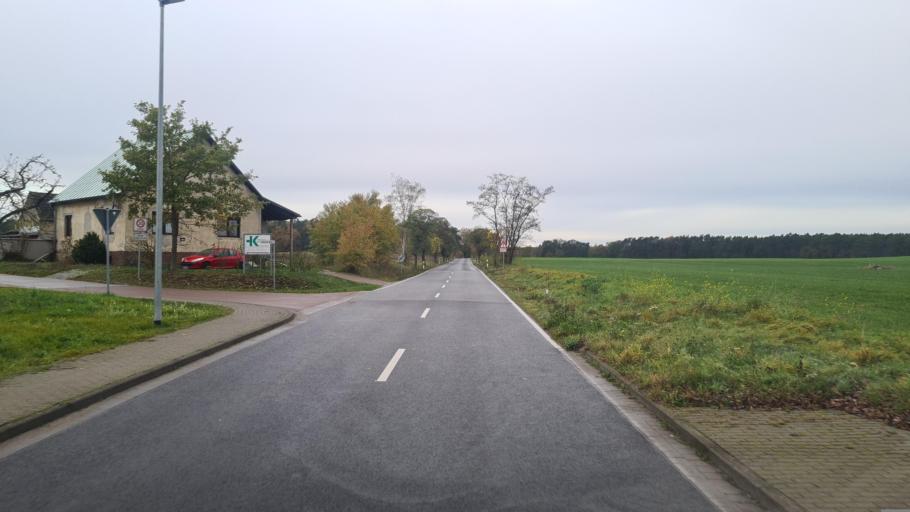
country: DE
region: Saxony-Anhalt
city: Abtsdorf
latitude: 51.9299
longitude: 12.6696
